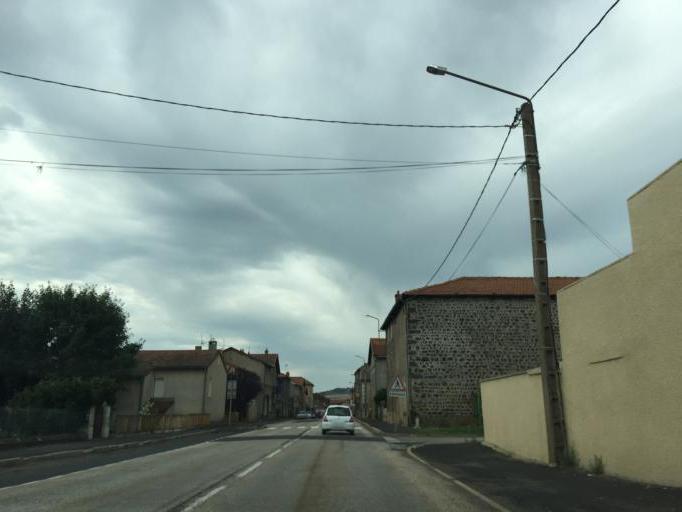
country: FR
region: Auvergne
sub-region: Departement de la Haute-Loire
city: Solignac-sur-Loire
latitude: 44.8967
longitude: 3.8501
